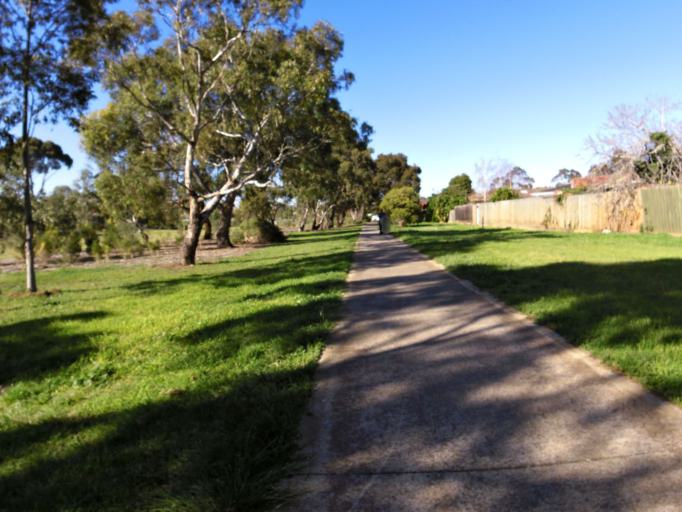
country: AU
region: Victoria
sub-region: Wyndham
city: Hoppers Crossing
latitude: -37.8854
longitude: 144.6860
